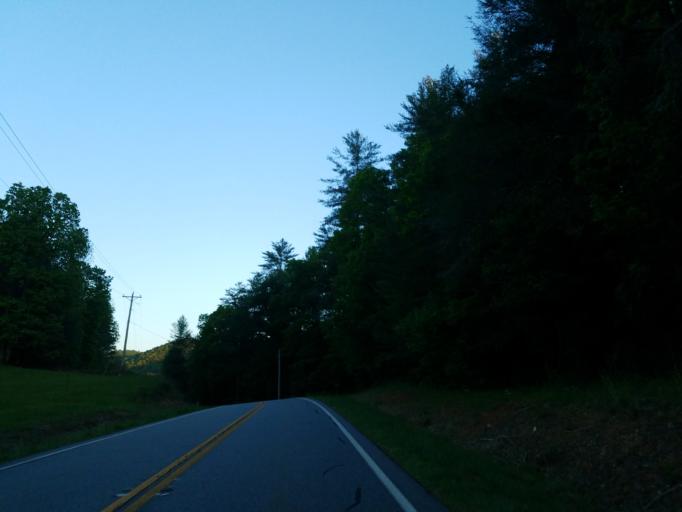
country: US
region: Georgia
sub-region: Union County
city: Blairsville
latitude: 34.7400
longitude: -84.1185
